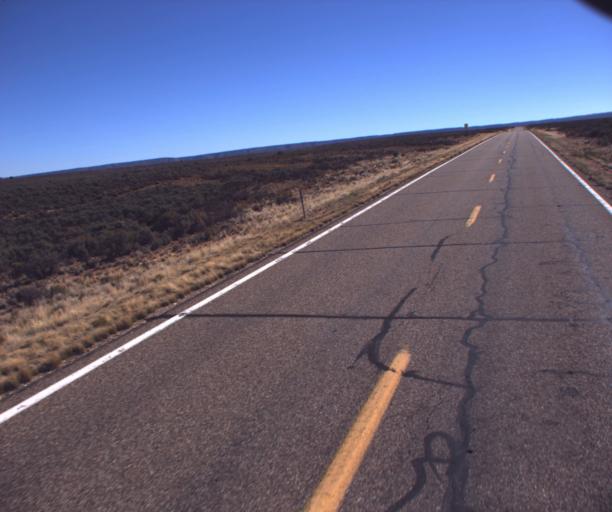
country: US
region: Arizona
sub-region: Coconino County
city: Fredonia
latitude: 36.9008
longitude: -112.3771
